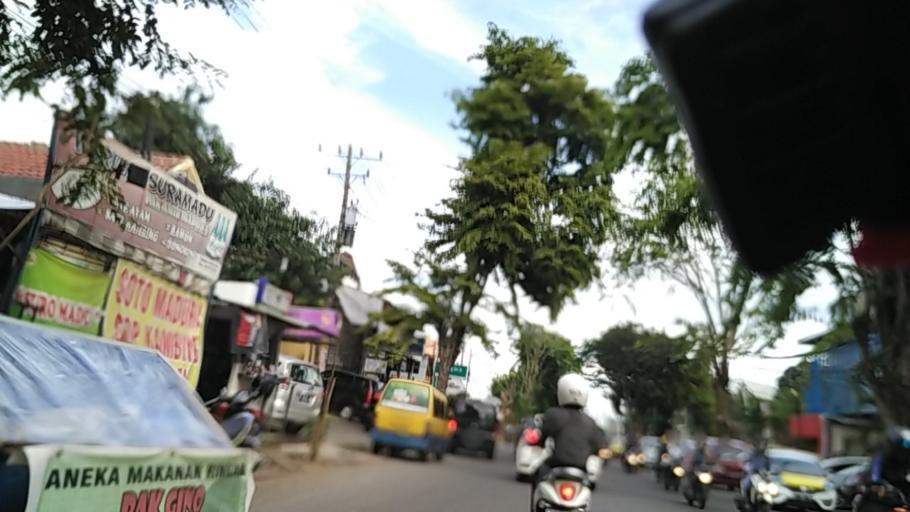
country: ID
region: Central Java
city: Semarang
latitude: -7.0499
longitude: 110.4223
